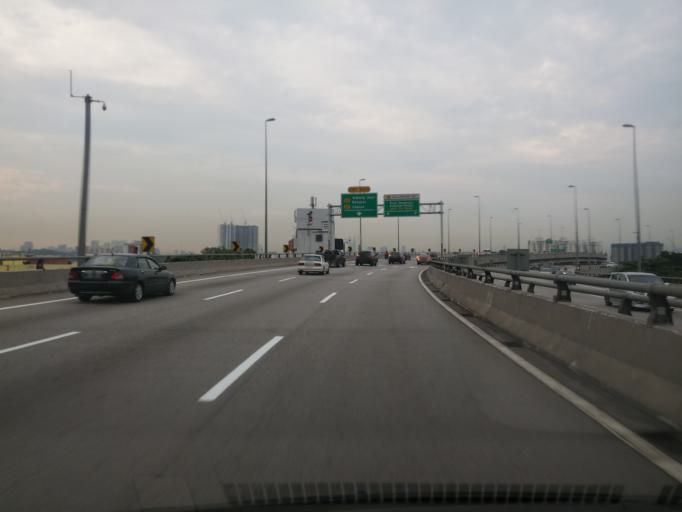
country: MY
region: Kuala Lumpur
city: Kuala Lumpur
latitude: 3.0871
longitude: 101.6941
